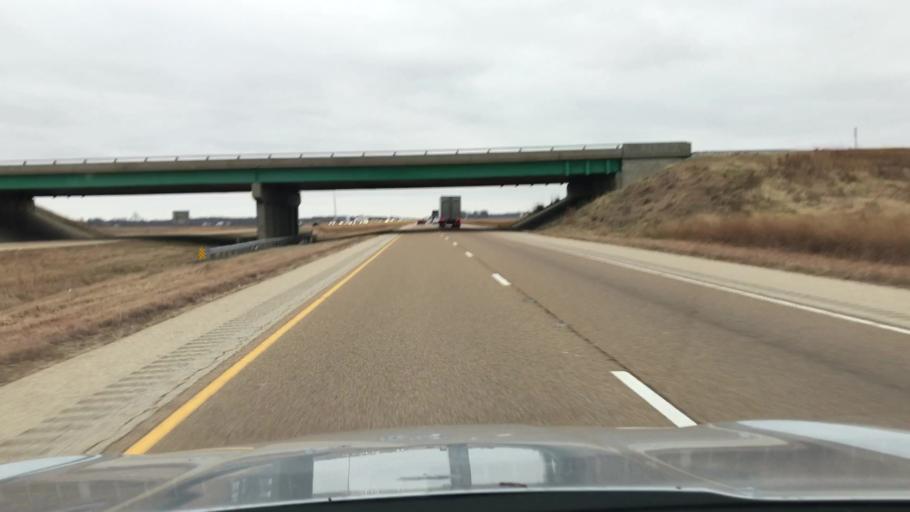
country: US
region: Illinois
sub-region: Montgomery County
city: Raymond
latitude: 39.3228
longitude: -89.6429
